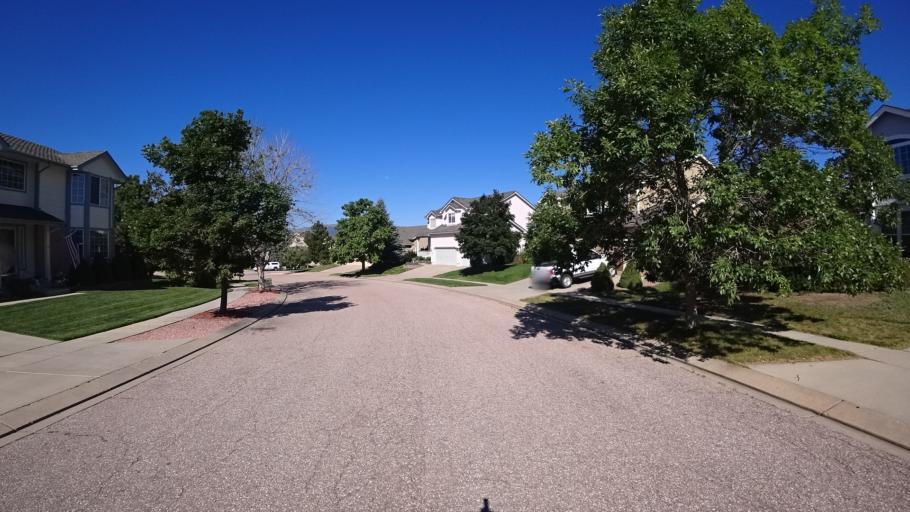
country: US
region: Colorado
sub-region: El Paso County
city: Gleneagle
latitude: 38.9773
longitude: -104.7811
